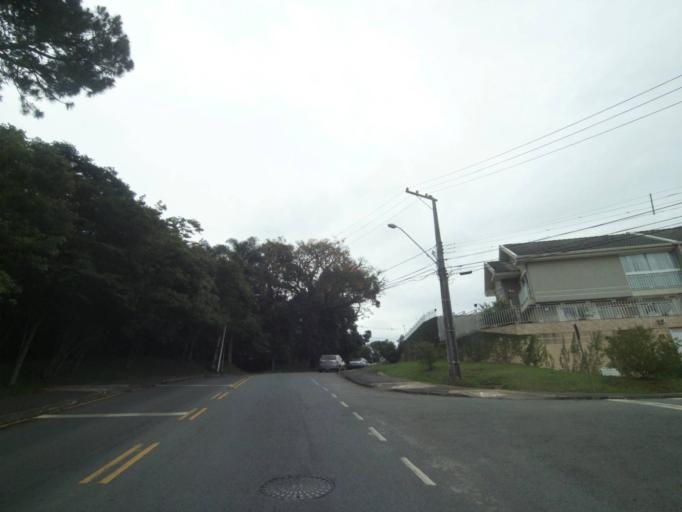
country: BR
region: Parana
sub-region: Curitiba
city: Curitiba
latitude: -25.3999
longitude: -49.2957
